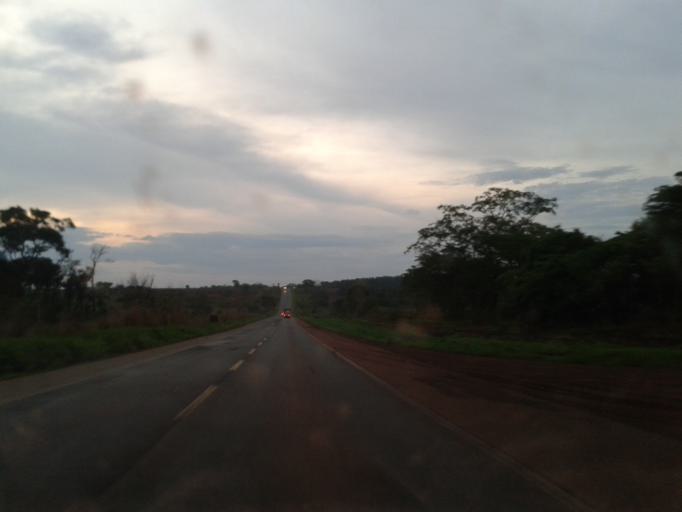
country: BR
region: Goias
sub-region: Santa Helena De Goias
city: Santa Helena de Goias
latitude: -17.8706
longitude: -50.7307
